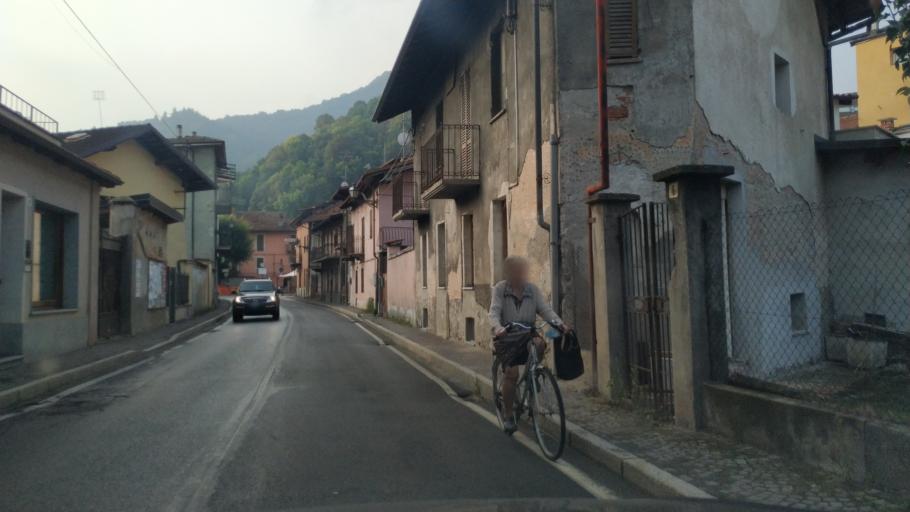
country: IT
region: Piedmont
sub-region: Provincia di Cuneo
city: Roccavione
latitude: 44.3161
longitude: 7.4821
